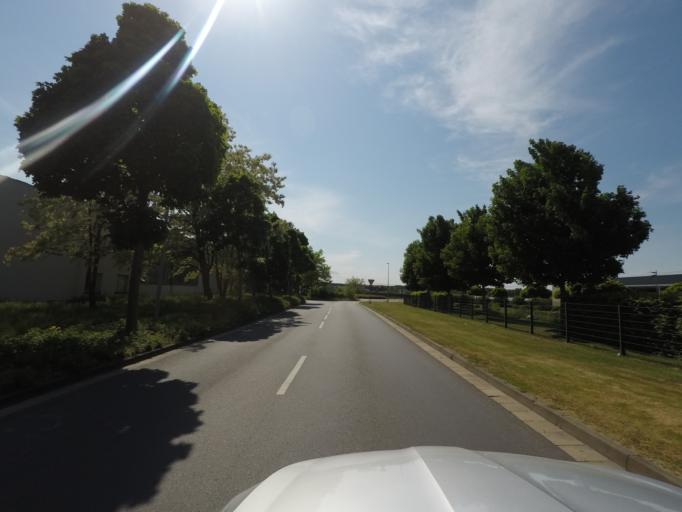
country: DE
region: Brandenburg
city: Britz
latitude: 52.8571
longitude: 13.7762
